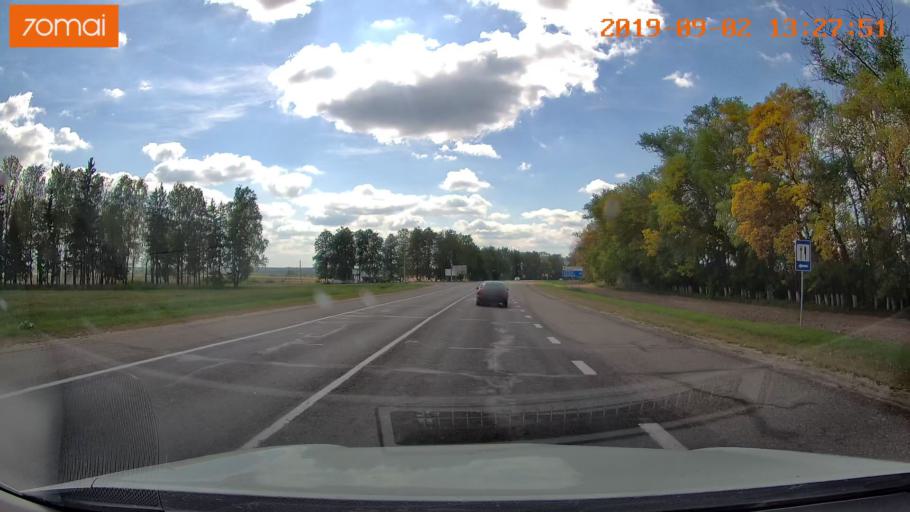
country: BY
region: Mogilev
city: Horad Krychaw
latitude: 53.6815
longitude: 31.6850
